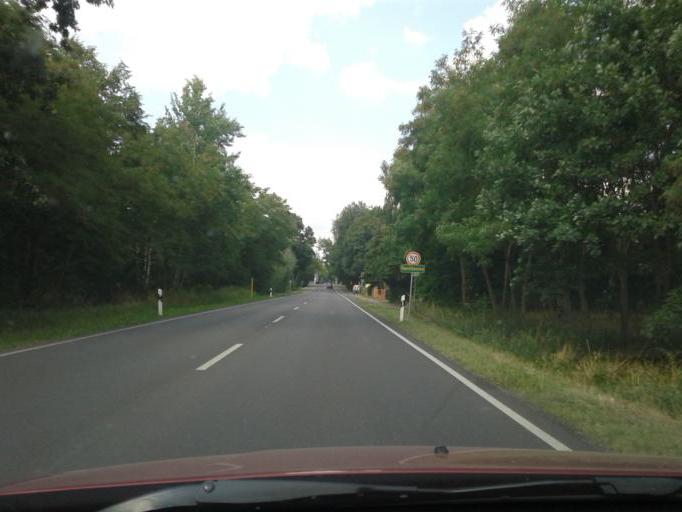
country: DE
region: Brandenburg
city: Oranienburg
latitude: 52.7203
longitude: 13.2527
